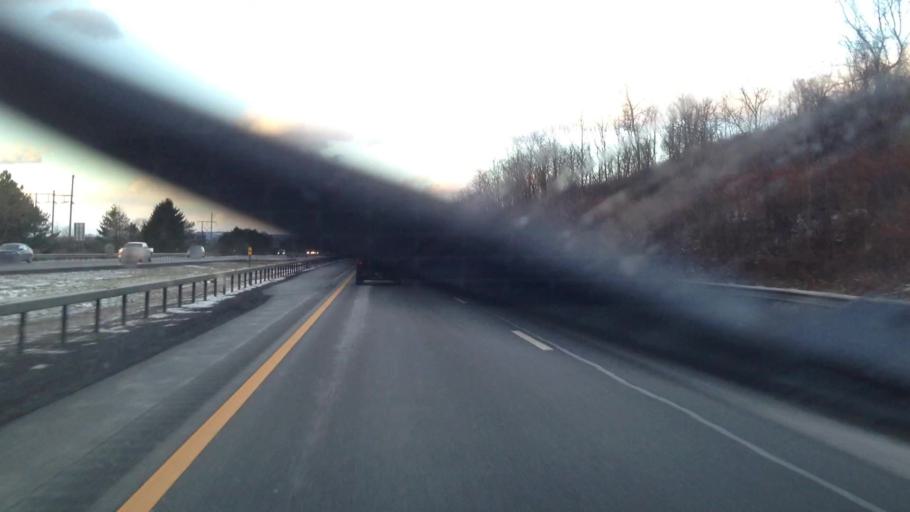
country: US
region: New York
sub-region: Herkimer County
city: Frankfort
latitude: 43.0359
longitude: -75.0483
